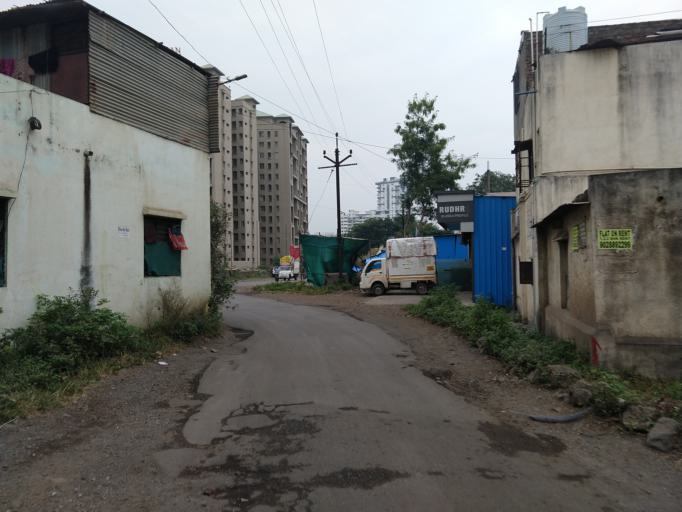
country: IN
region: Maharashtra
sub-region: Pune Division
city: Pune
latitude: 18.4546
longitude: 73.8846
